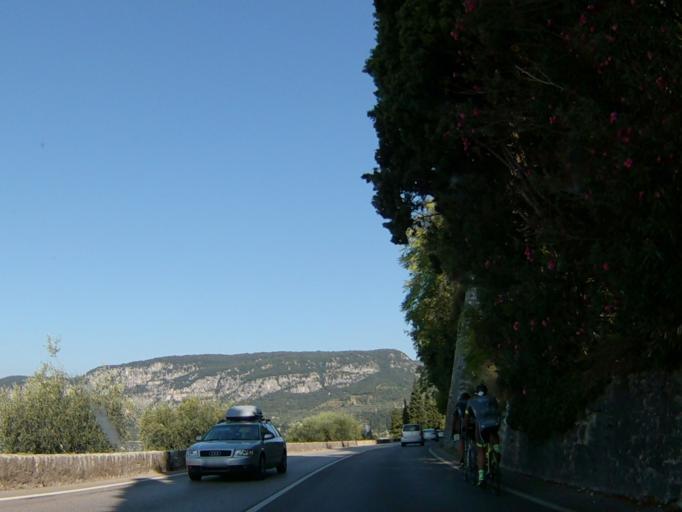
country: IT
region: Veneto
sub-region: Provincia di Verona
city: Garda
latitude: 45.5676
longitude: 10.7094
